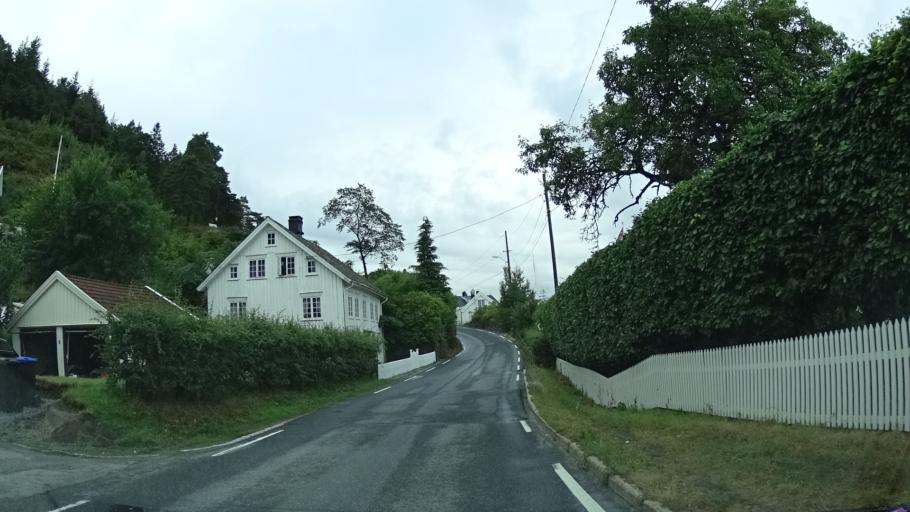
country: NO
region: Aust-Agder
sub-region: Arendal
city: Arendal
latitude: 58.4499
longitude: 8.7545
